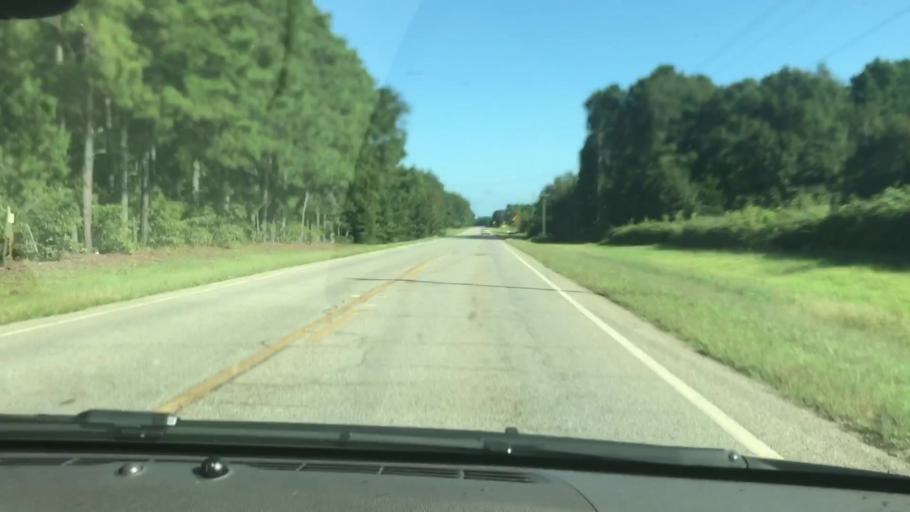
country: US
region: Georgia
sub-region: Clay County
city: Fort Gaines
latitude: 31.7272
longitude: -85.0456
